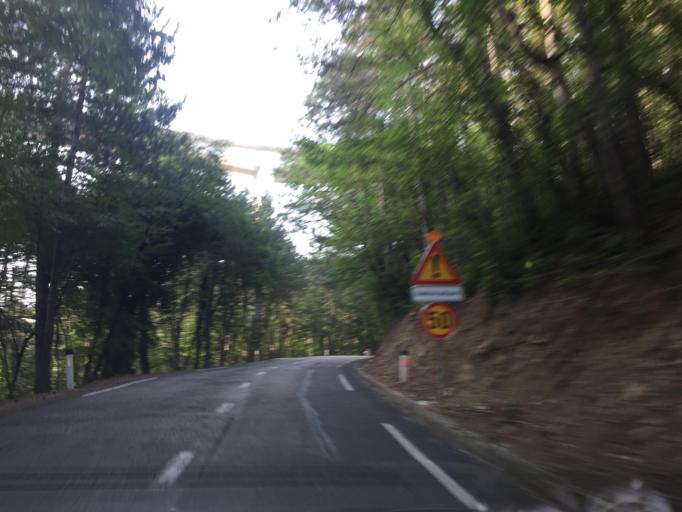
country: IT
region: Friuli Venezia Giulia
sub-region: Provincia di Trieste
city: Dolina
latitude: 45.5565
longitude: 13.8671
